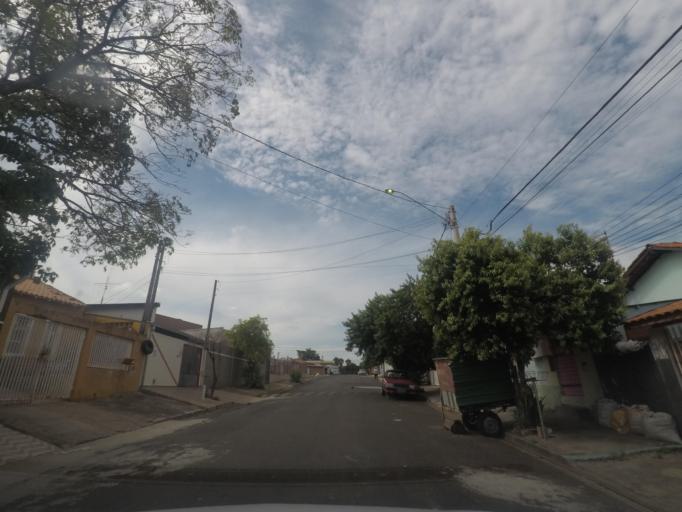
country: BR
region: Sao Paulo
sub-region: Sumare
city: Sumare
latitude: -22.8078
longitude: -47.2636
